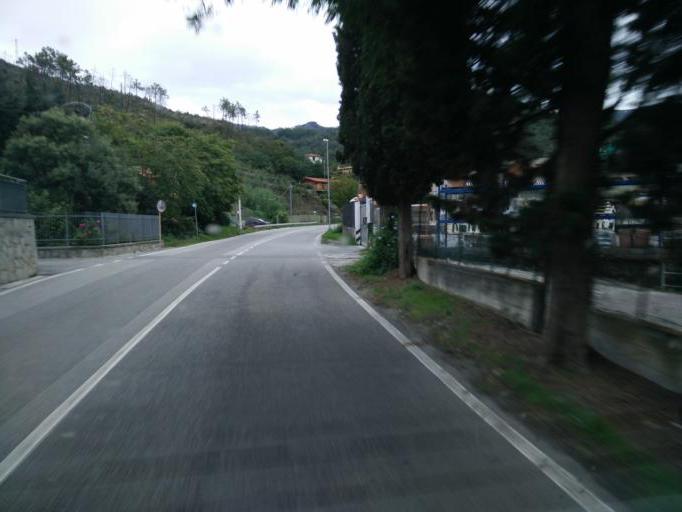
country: IT
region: Liguria
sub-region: Provincia di La Spezia
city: Framura
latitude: 44.2264
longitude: 9.5462
